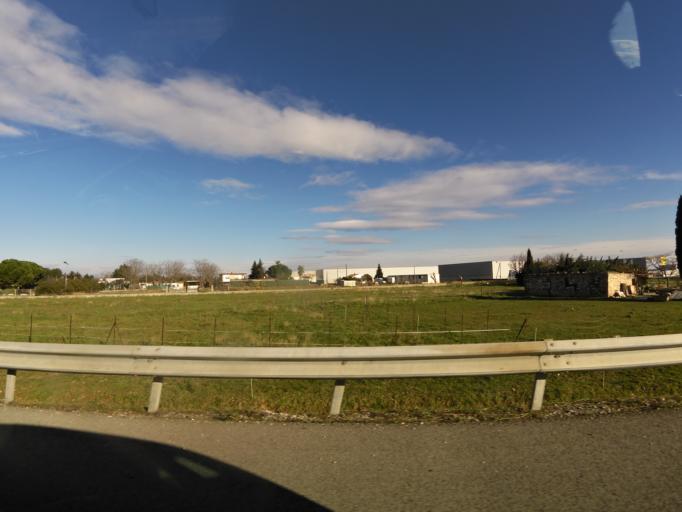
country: FR
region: Languedoc-Roussillon
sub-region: Departement du Gard
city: Milhaud
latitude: 43.7971
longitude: 4.3175
